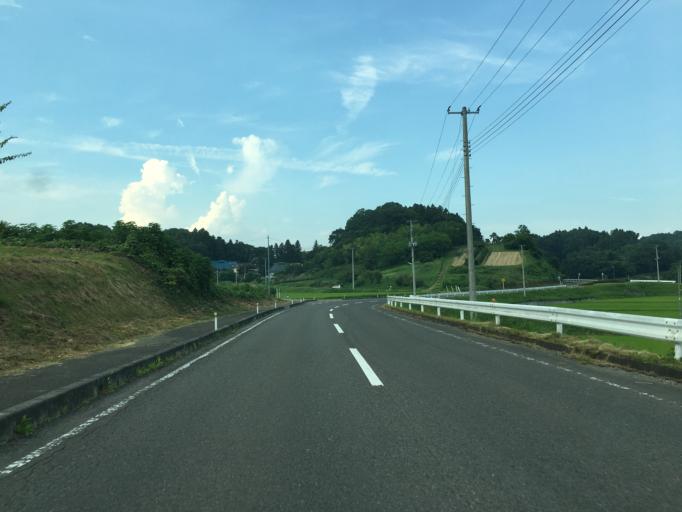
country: JP
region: Fukushima
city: Motomiya
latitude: 37.5152
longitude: 140.4421
